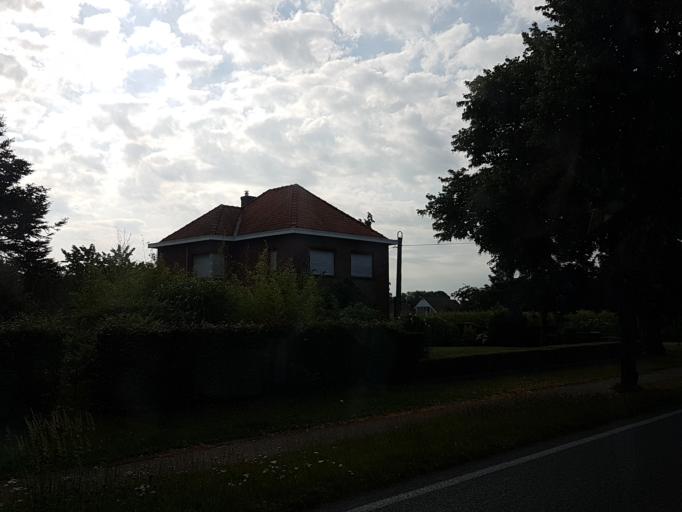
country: BE
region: Flanders
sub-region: Provincie Antwerpen
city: Olen
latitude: 51.1325
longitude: 4.8651
